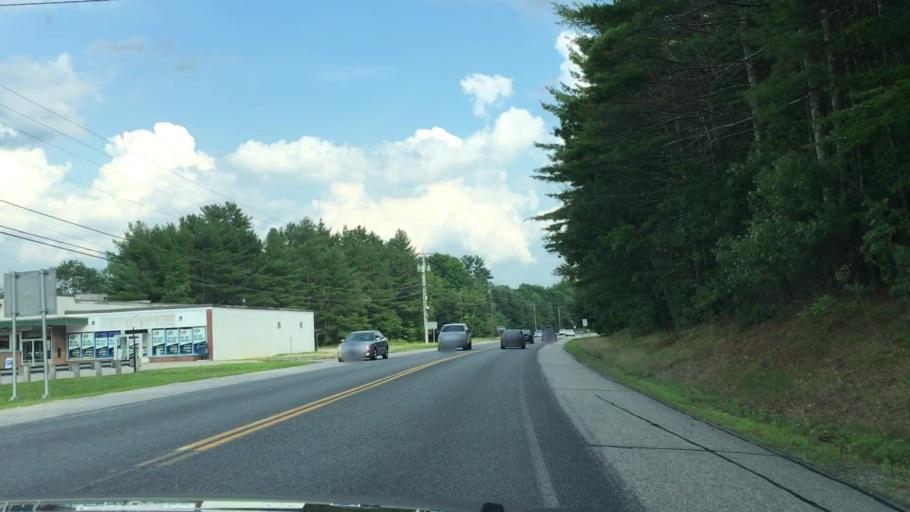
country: US
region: New Hampshire
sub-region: Strafford County
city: Farmington
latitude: 43.3847
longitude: -71.0746
